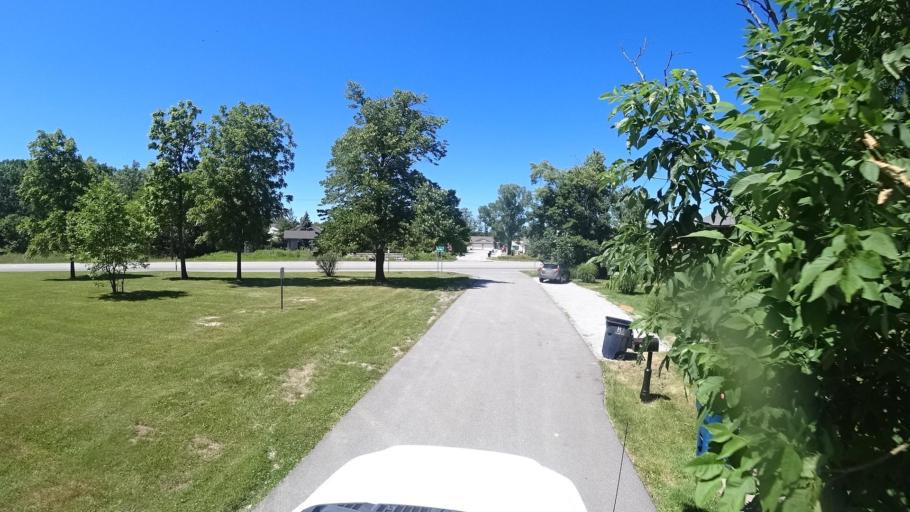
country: US
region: Indiana
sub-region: Porter County
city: Porter
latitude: 41.6308
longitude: -87.0685
